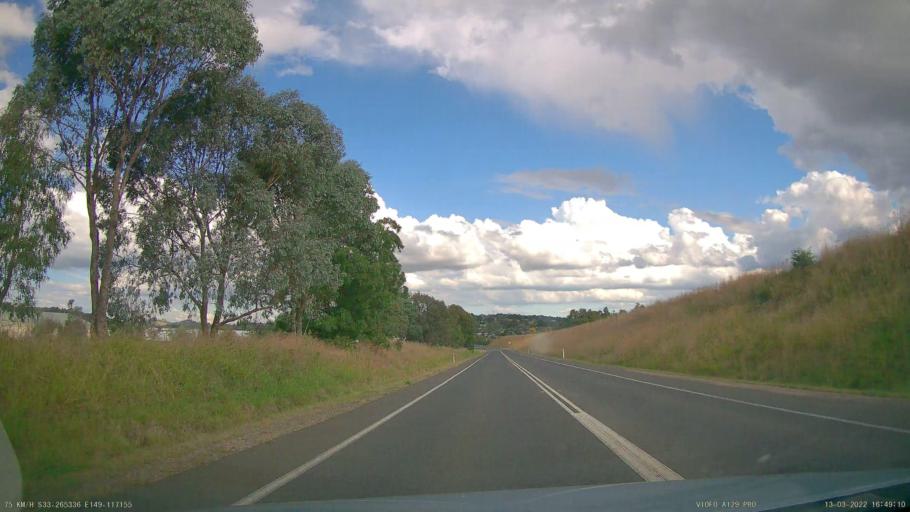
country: AU
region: New South Wales
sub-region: Orange Municipality
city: Orange
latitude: -33.2655
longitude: 149.1171
